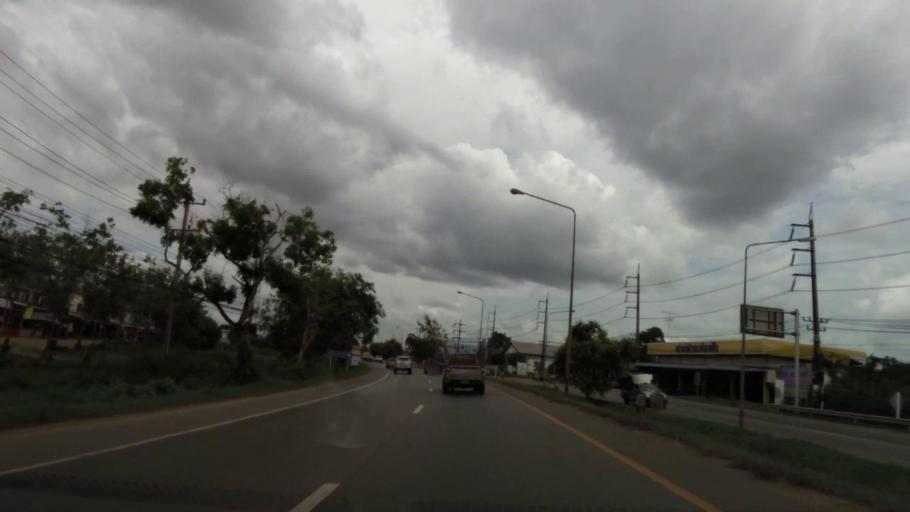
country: TH
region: Rayong
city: Klaeng
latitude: 12.7868
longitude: 101.6624
